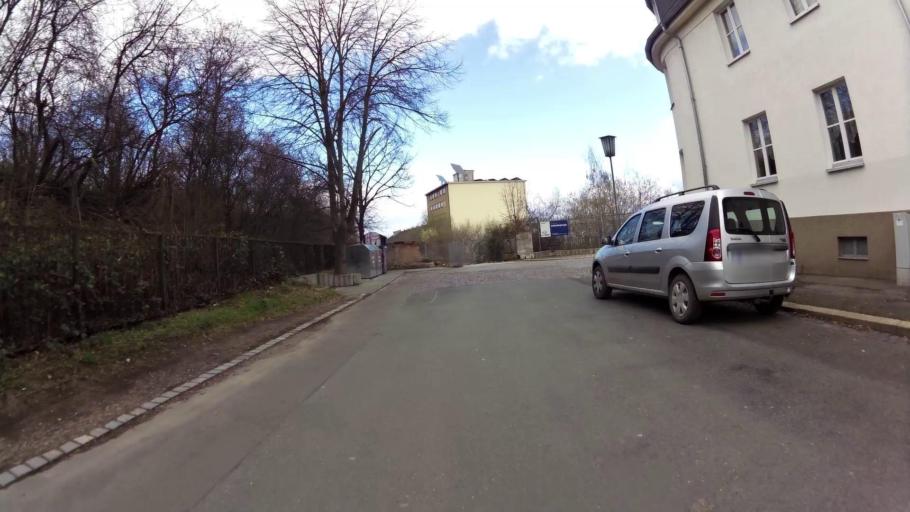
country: DE
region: Thuringia
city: Weimar
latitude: 50.9902
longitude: 11.3339
